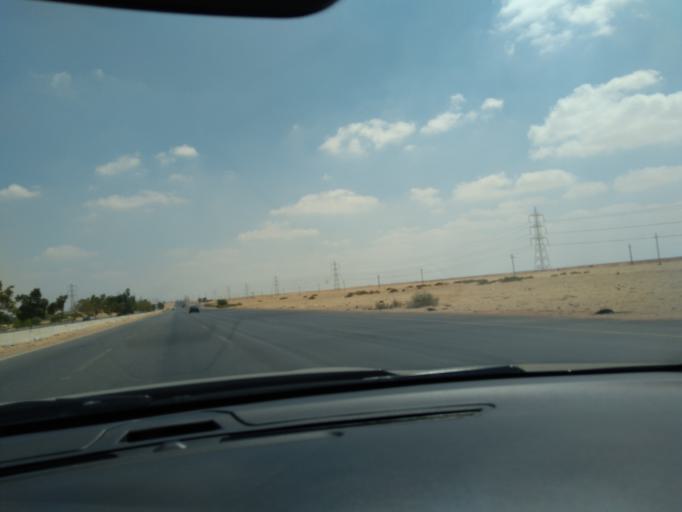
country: EG
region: Al Isma'iliyah
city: At Tall al Kabir
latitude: 30.3627
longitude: 31.9093
